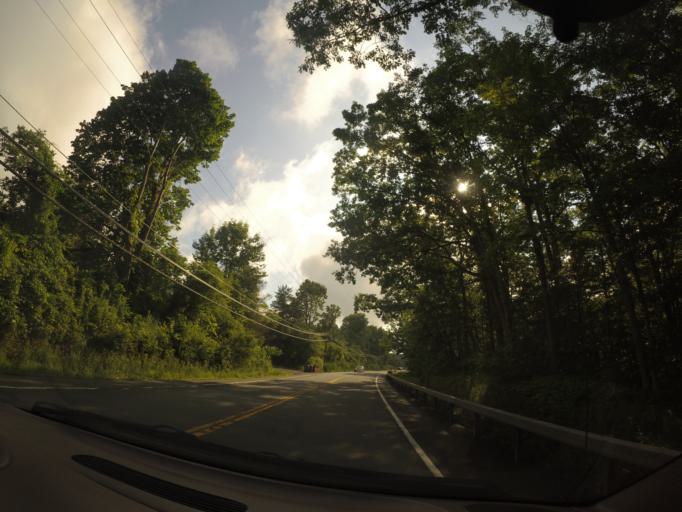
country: US
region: New York
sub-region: Rensselaer County
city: Poestenkill
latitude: 42.8226
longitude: -73.5102
